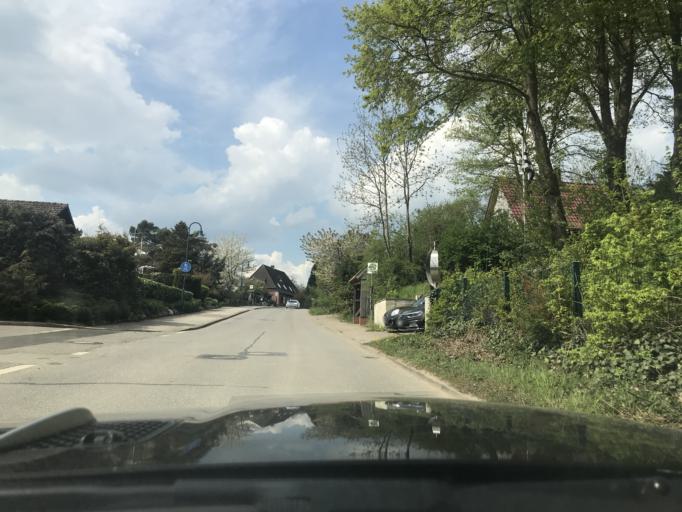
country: DE
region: Schleswig-Holstein
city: Schashagen
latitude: 54.0987
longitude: 10.8837
